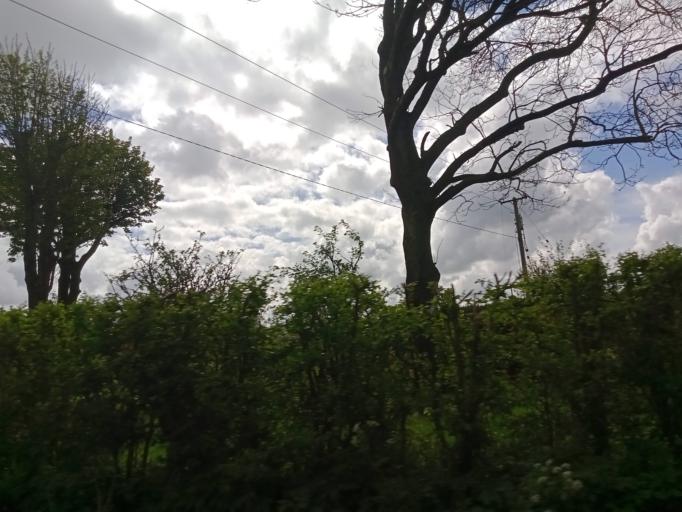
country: IE
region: Munster
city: Thurles
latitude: 52.6935
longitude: -7.6400
